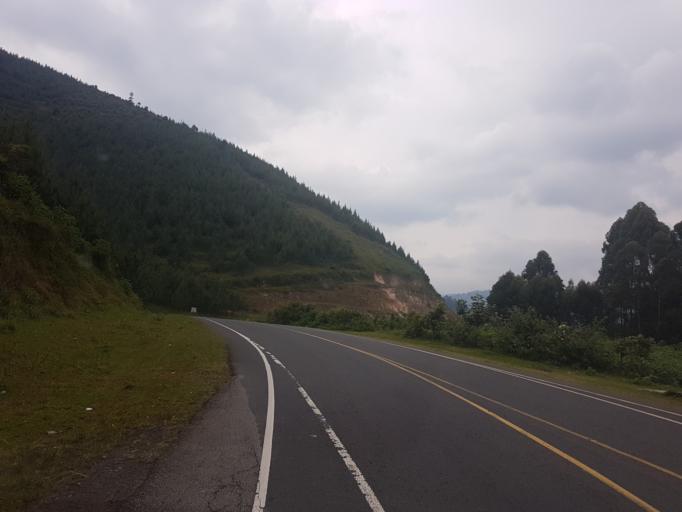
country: UG
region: Western Region
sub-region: Kabale District
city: Kabale
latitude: -1.2086
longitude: 29.8322
